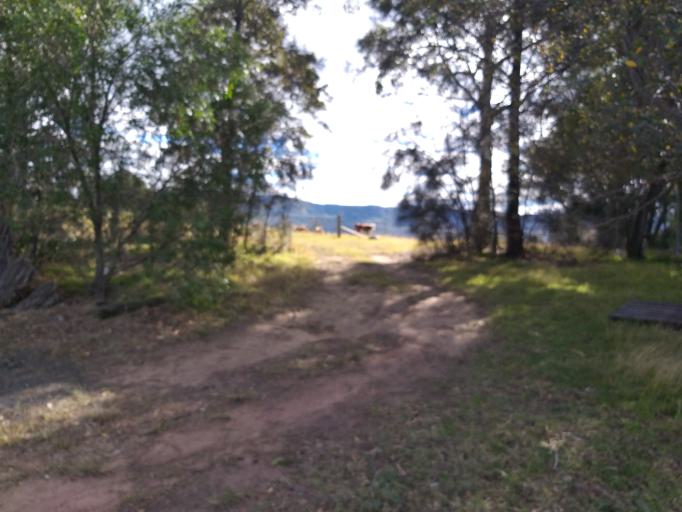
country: AU
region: New South Wales
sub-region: Wollongong
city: Dapto
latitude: -34.5206
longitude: 150.7714
